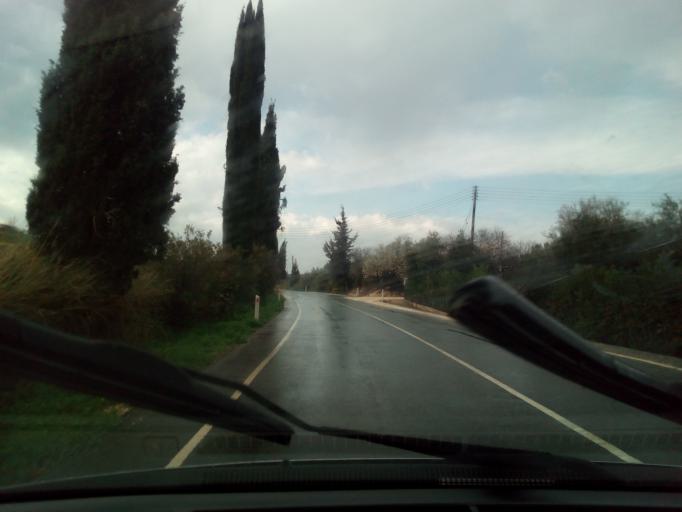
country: CY
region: Pafos
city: Polis
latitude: 35.0159
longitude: 32.4502
